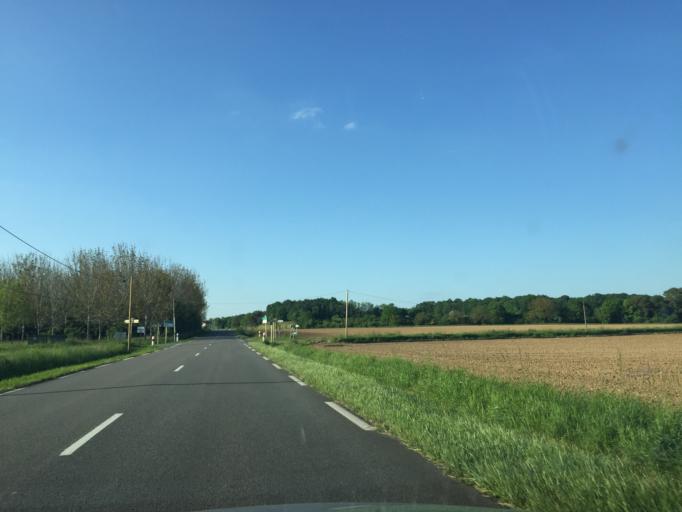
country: FR
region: Poitou-Charentes
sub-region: Departement de la Charente
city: Chalais
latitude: 45.2181
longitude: 0.0338
